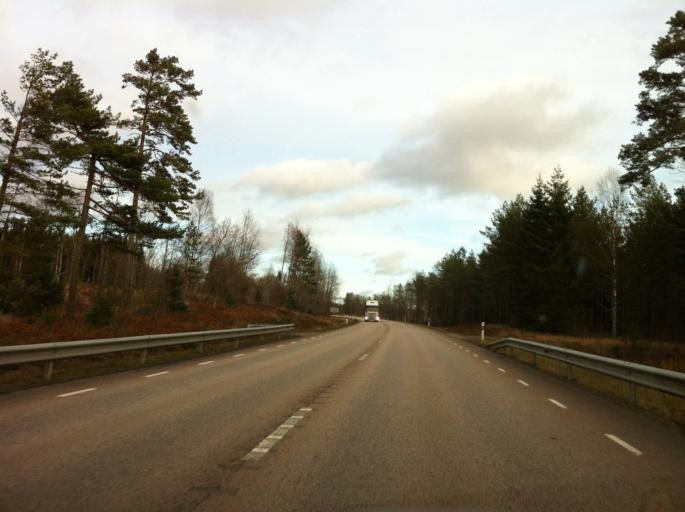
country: SE
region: Kronoberg
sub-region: Uppvidinge Kommun
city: Lenhovda
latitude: 57.1092
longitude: 15.2091
